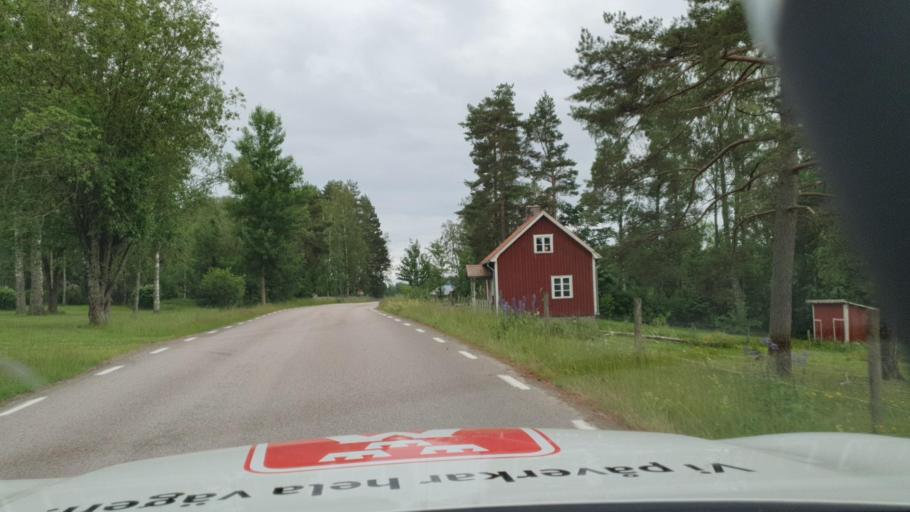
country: SE
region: Vaermland
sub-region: Sunne Kommun
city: Sunne
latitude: 59.7156
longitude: 13.2273
